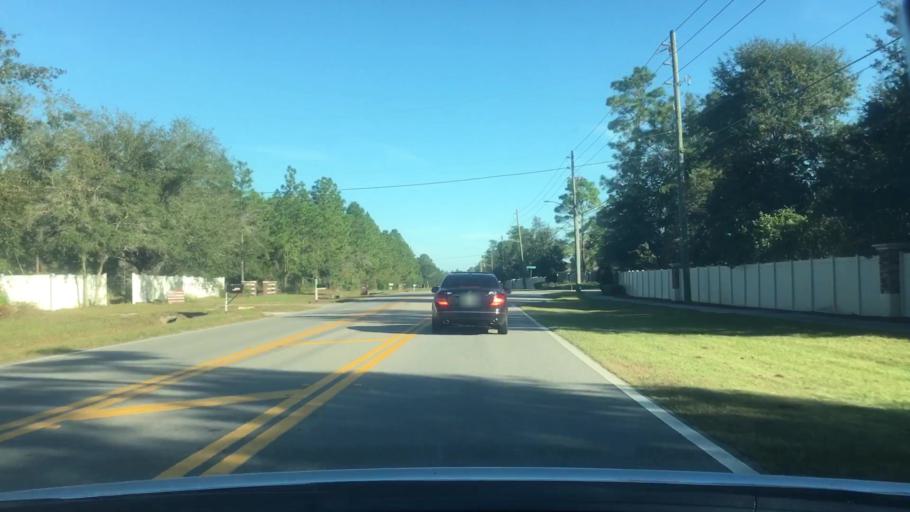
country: US
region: Florida
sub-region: Nassau County
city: Yulee
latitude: 30.4900
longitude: -81.5755
